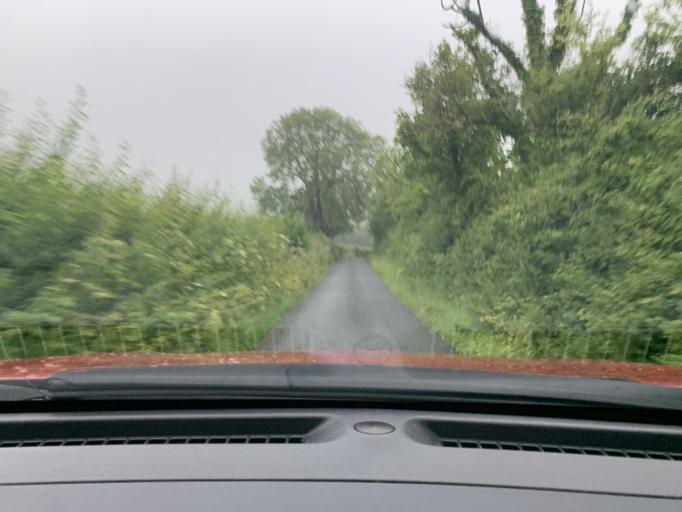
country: IE
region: Connaught
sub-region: Sligo
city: Sligo
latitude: 54.3227
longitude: -8.4489
